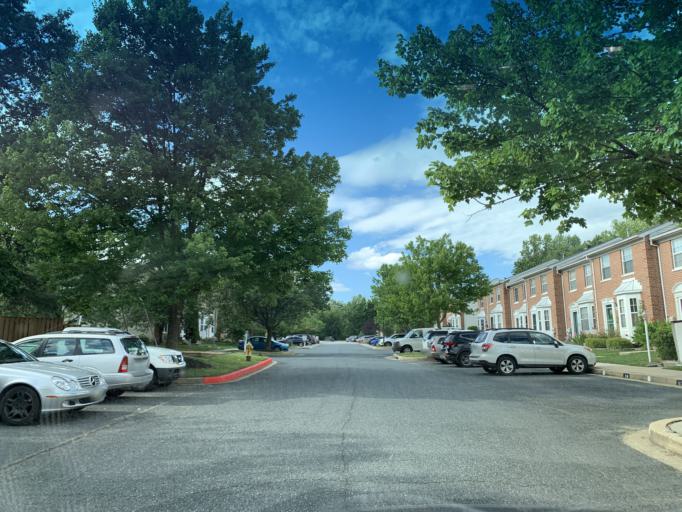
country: US
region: Maryland
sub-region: Harford County
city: Riverside
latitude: 39.4826
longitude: -76.2415
